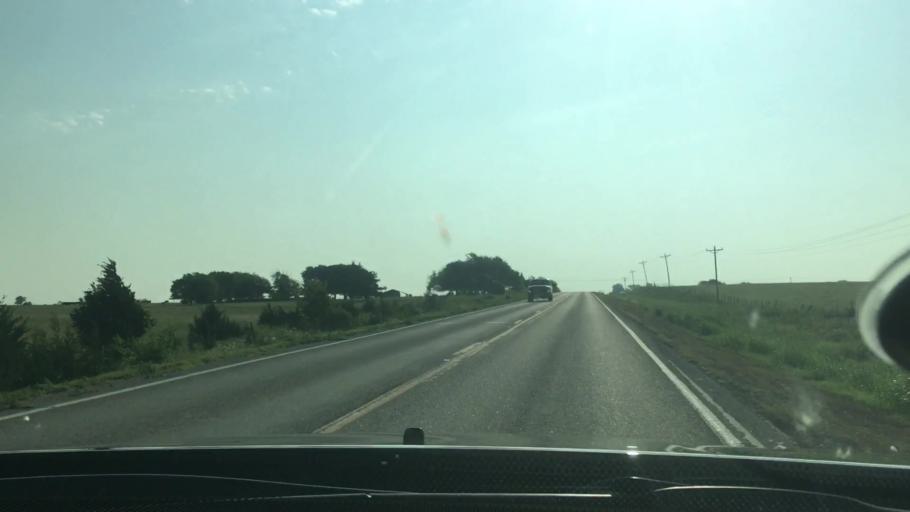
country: US
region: Oklahoma
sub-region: Bryan County
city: Durant
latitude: 34.1427
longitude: -96.3259
